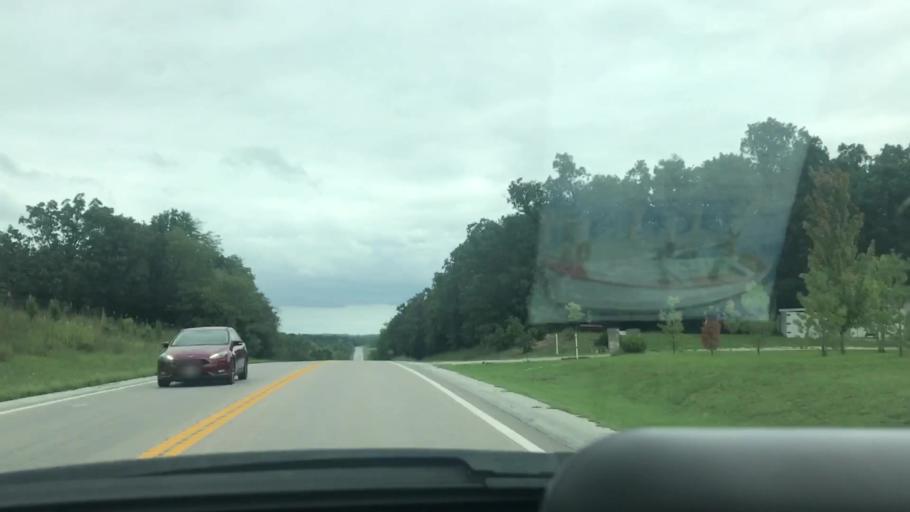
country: US
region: Missouri
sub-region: Dallas County
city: Buffalo
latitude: 37.7127
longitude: -93.1163
